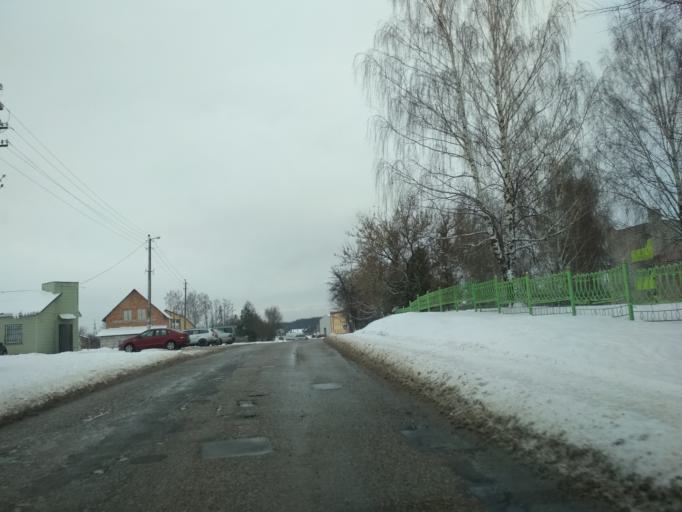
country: BY
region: Minsk
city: Mar''ina Horka
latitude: 53.5255
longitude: 28.1391
